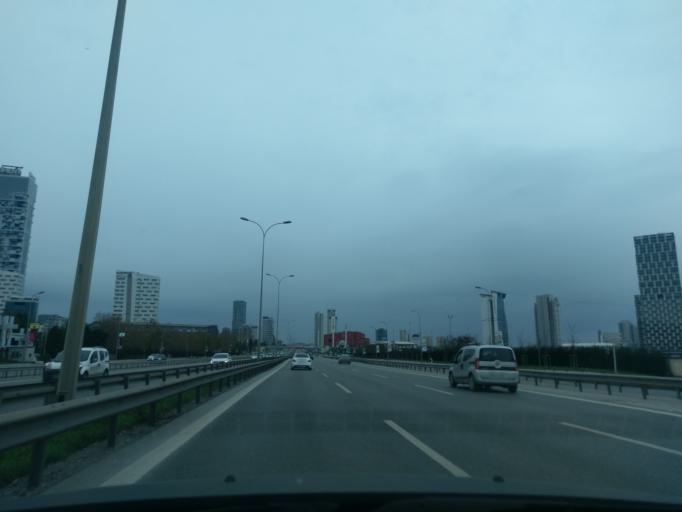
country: TR
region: Istanbul
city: Maltepe
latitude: 40.9155
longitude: 29.1828
